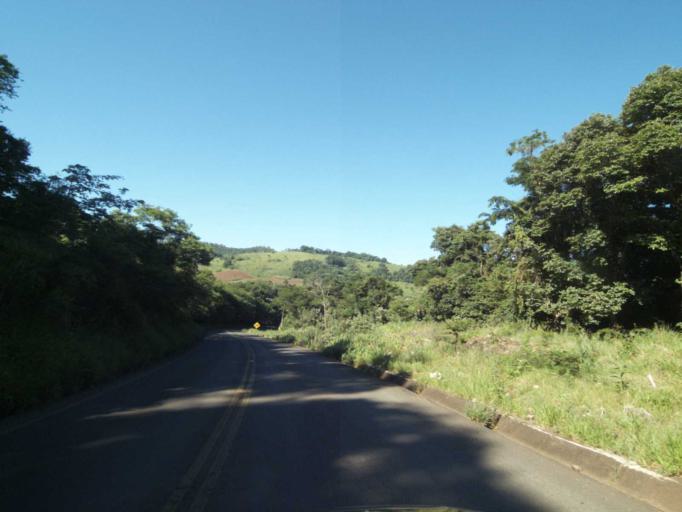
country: BR
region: Parana
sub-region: Francisco Beltrao
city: Francisco Beltrao
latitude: -26.1433
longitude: -53.3034
